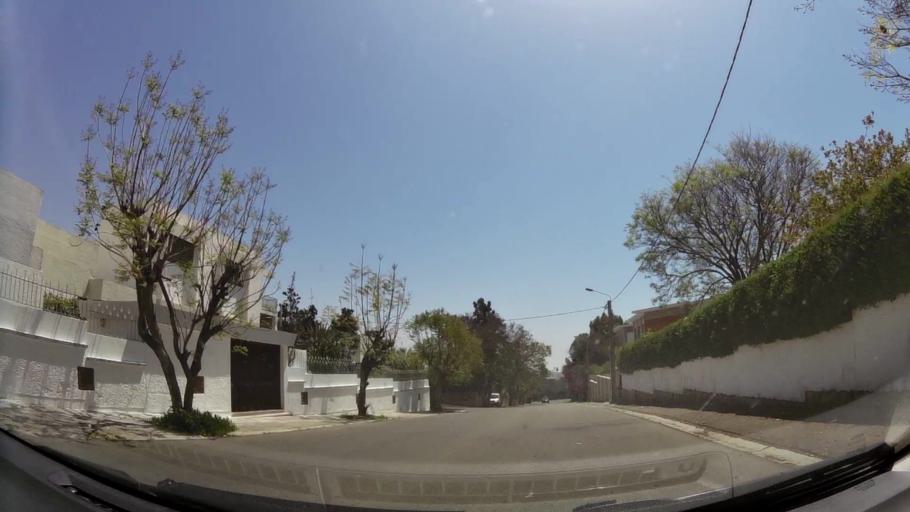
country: MA
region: Souss-Massa-Draa
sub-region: Agadir-Ida-ou-Tnan
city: Agadir
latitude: 30.4290
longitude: -9.5970
